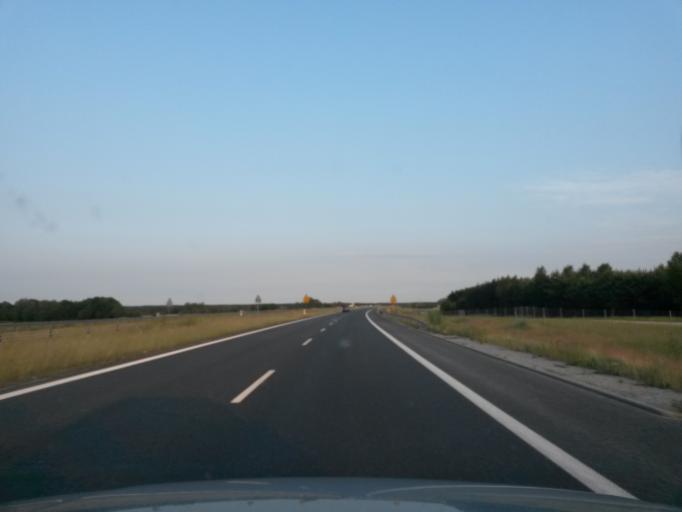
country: PL
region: Lodz Voivodeship
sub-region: Powiat wieruszowski
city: Wieruszow
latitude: 51.3314
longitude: 18.1454
